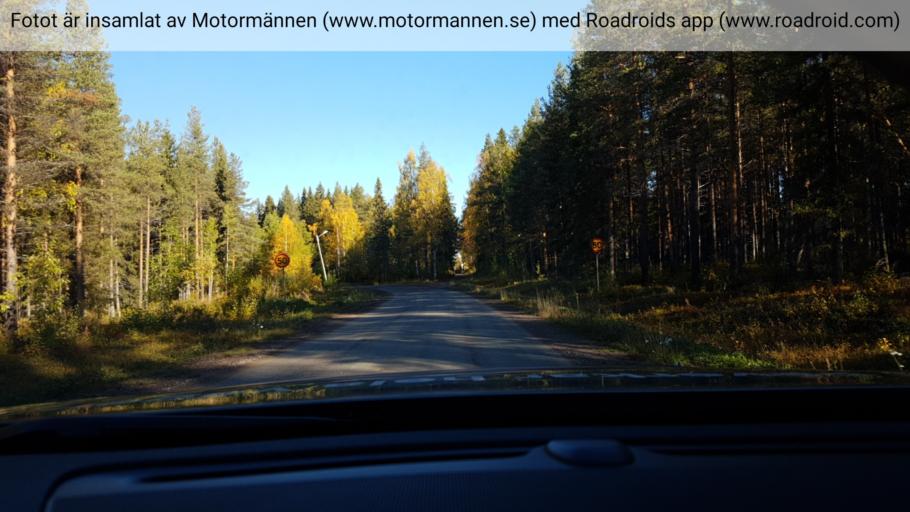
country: SE
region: Norrbotten
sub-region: Alvsbyns Kommun
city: AElvsbyn
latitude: 66.2686
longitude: 21.1256
